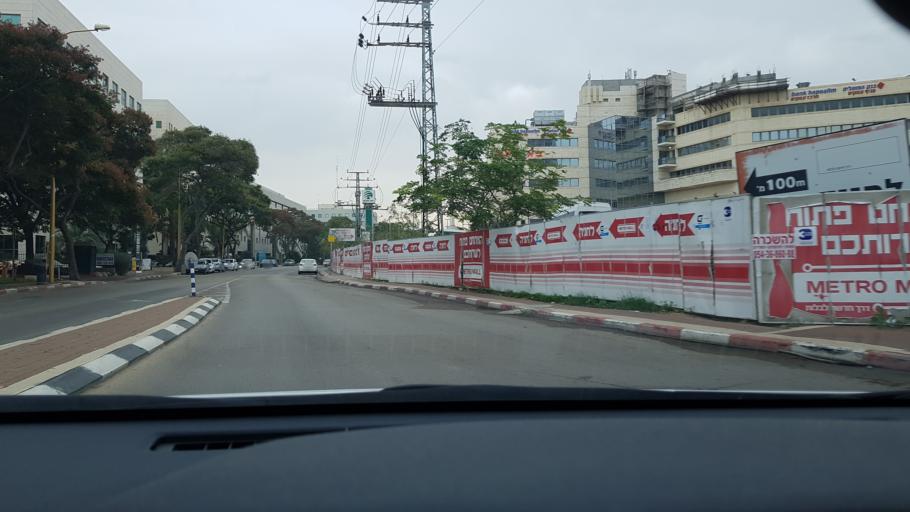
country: IL
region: Central District
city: Ness Ziona
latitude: 31.9104
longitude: 34.8059
